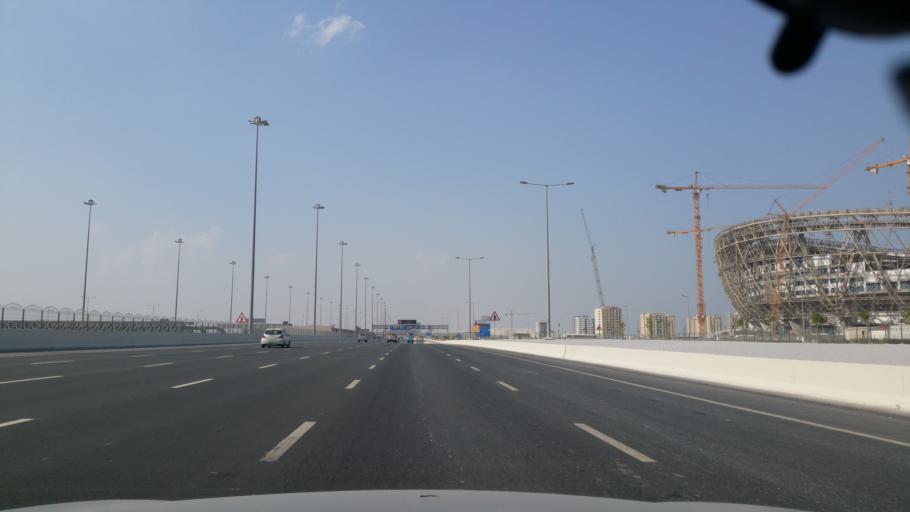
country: QA
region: Baladiyat Umm Salal
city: Umm Salal Muhammad
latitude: 25.4162
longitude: 51.4879
